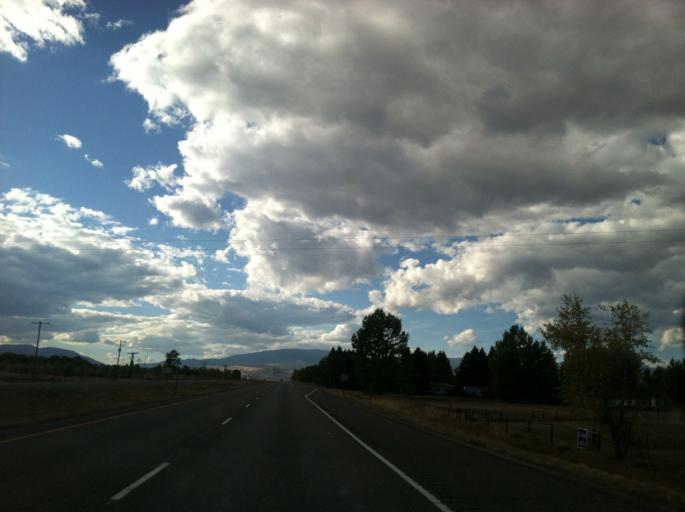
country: US
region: Montana
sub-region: Deer Lodge County
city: Warm Springs
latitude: 46.1060
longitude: -112.8462
